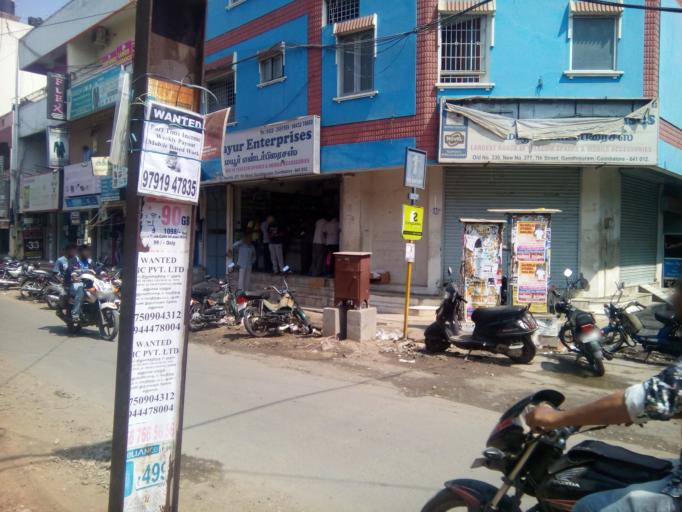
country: IN
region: Tamil Nadu
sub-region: Coimbatore
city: Coimbatore
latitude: 11.0189
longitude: 76.9660
